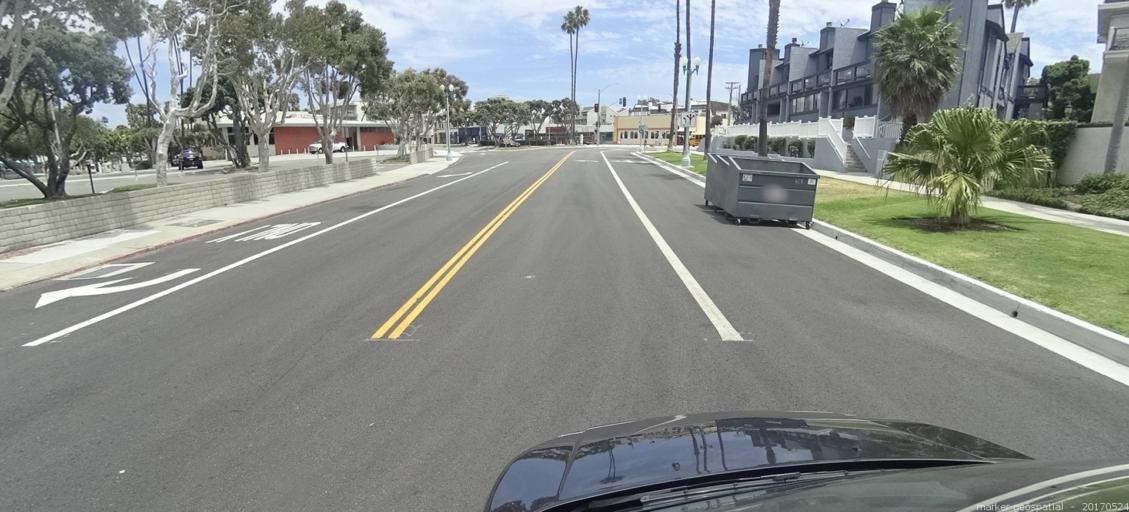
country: US
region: California
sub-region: Los Angeles County
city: Redondo Beach
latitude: 33.8362
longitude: -118.3887
